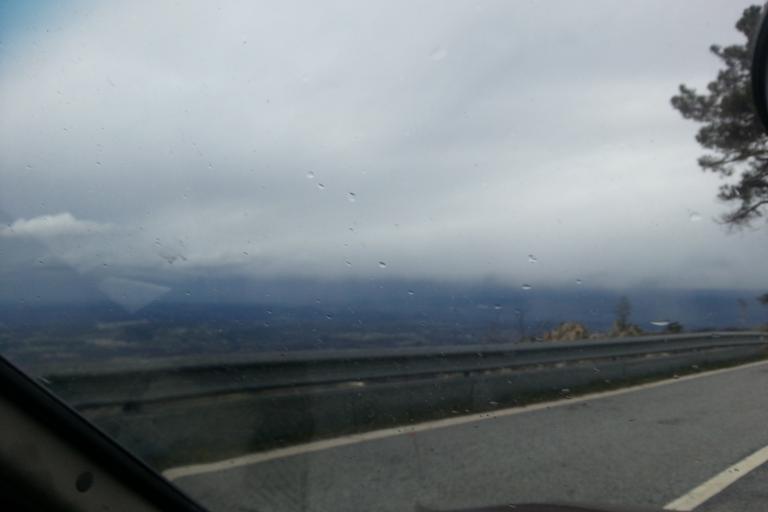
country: PT
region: Guarda
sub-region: Manteigas
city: Manteigas
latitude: 40.4496
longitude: -7.6002
